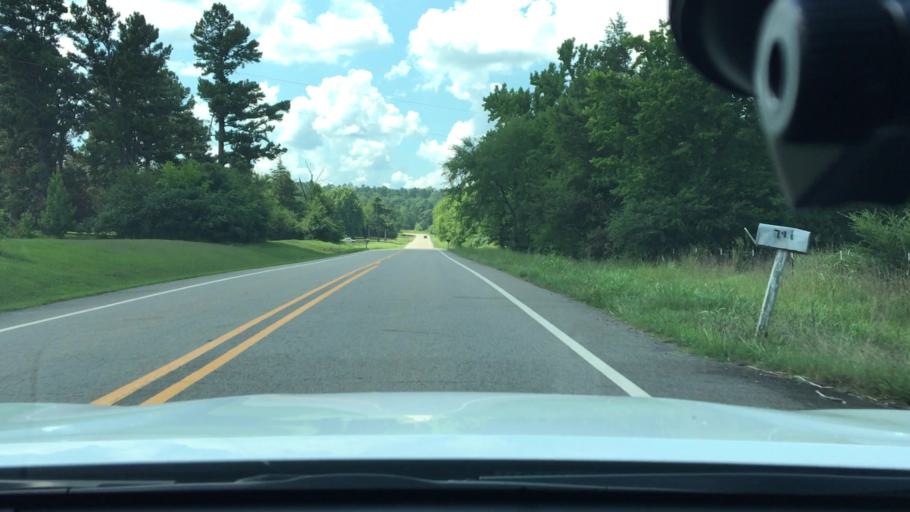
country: US
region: Arkansas
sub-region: Logan County
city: Paris
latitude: 35.2636
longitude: -93.6832
